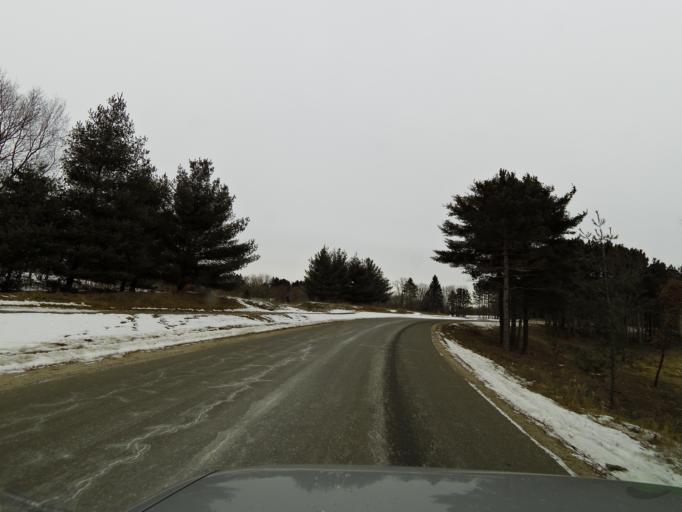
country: US
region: Minnesota
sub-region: Washington County
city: Lake Elmo
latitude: 44.9743
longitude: -92.9047
